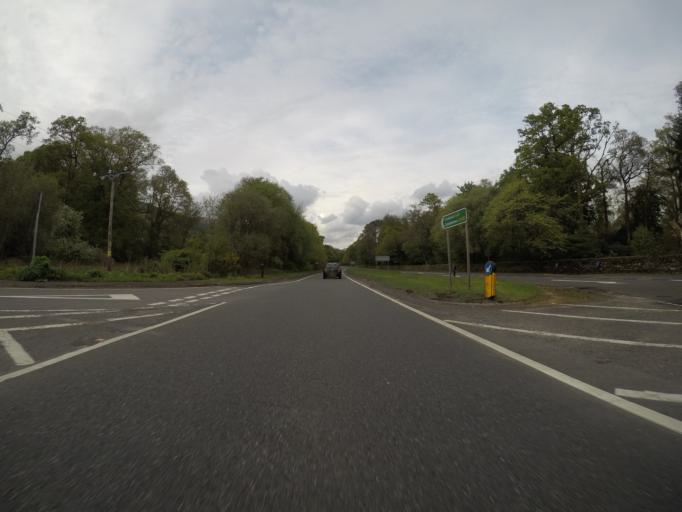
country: GB
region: Scotland
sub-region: West Dunbartonshire
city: Balloch
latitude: 56.0591
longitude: -4.6461
